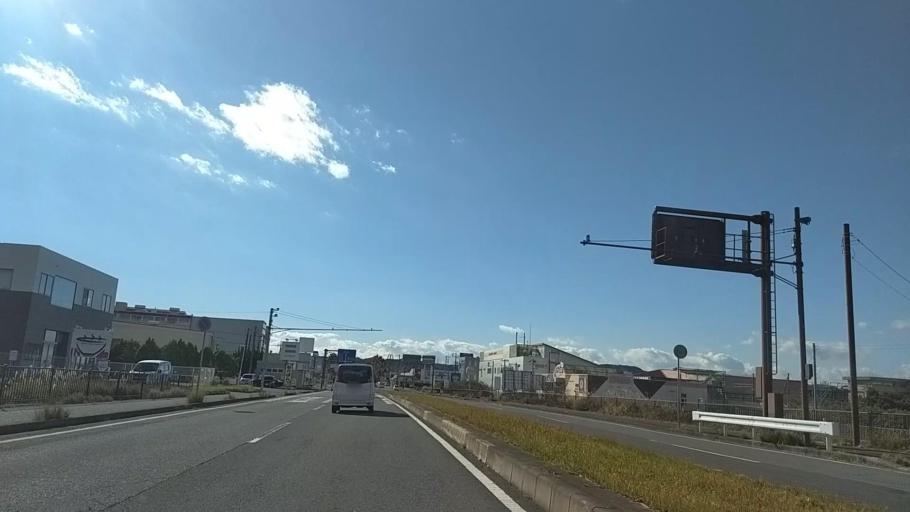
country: JP
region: Chiba
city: Tateyama
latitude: 34.9938
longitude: 139.8741
